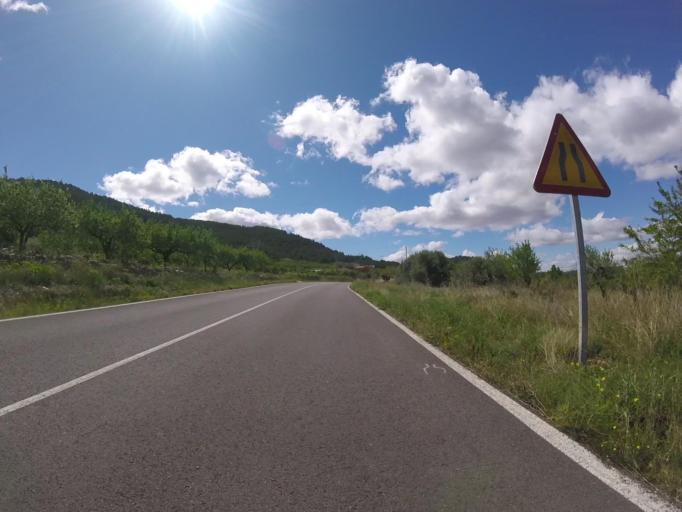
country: ES
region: Valencia
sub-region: Provincia de Castello
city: Culla
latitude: 40.2844
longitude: -0.1126
